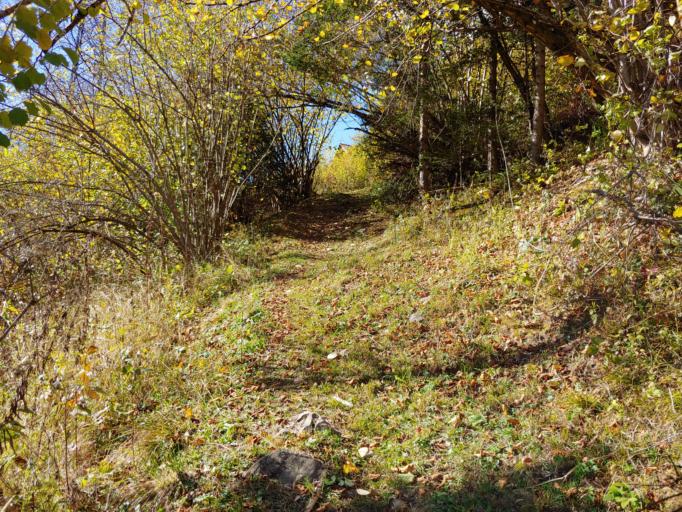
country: IT
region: Veneto
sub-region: Provincia di Belluno
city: Lozzo di Cadore
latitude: 46.4917
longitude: 12.4485
